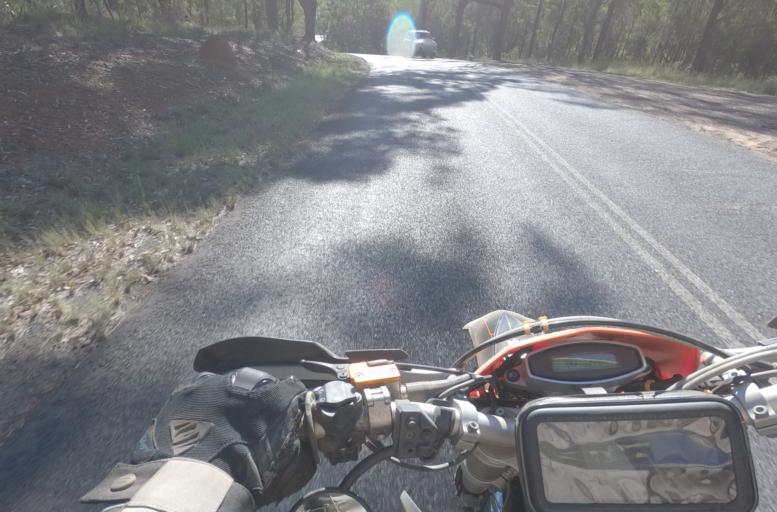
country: AU
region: New South Wales
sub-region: Hawkesbury
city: Scheyville
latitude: -33.5828
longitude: 150.8842
